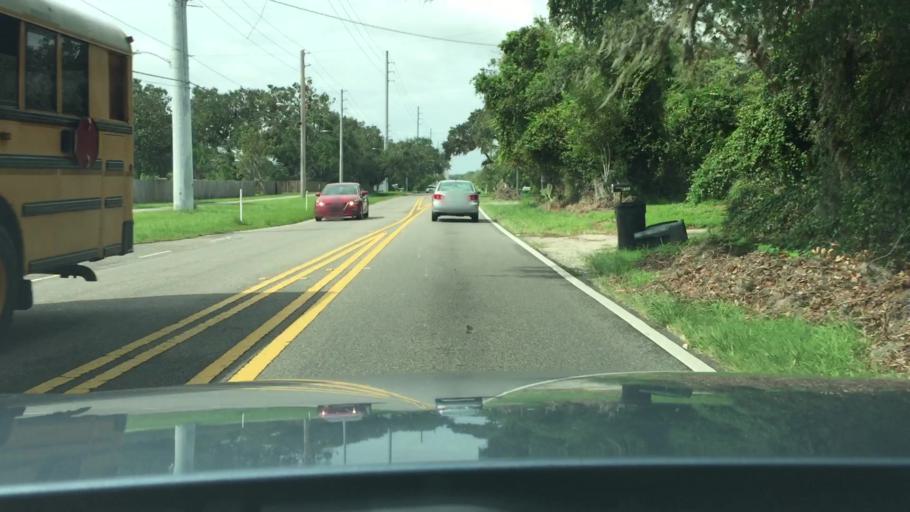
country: US
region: Florida
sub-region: Osceola County
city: Buenaventura Lakes
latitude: 28.2675
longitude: -81.3495
